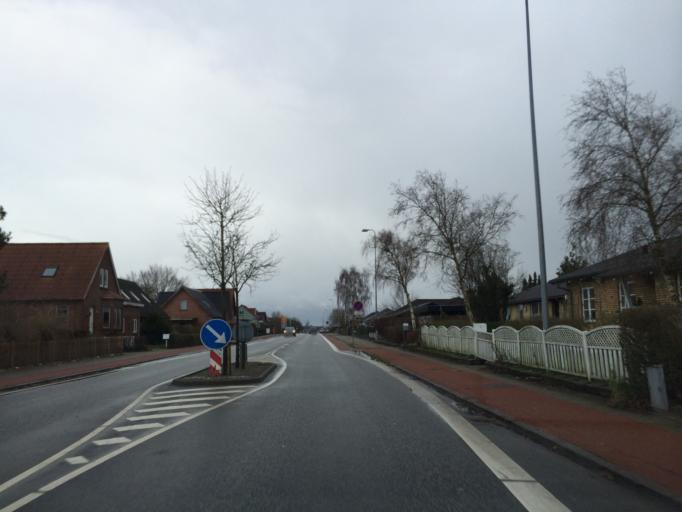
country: DK
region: Central Jutland
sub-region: Ringkobing-Skjern Kommune
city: Skjern
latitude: 55.9379
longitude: 8.5036
